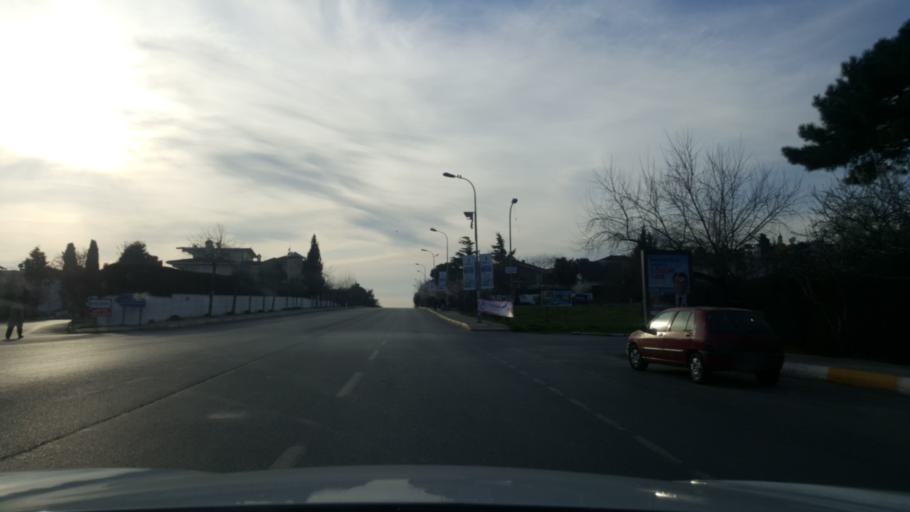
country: TR
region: Istanbul
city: Icmeler
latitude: 40.8180
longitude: 29.2837
